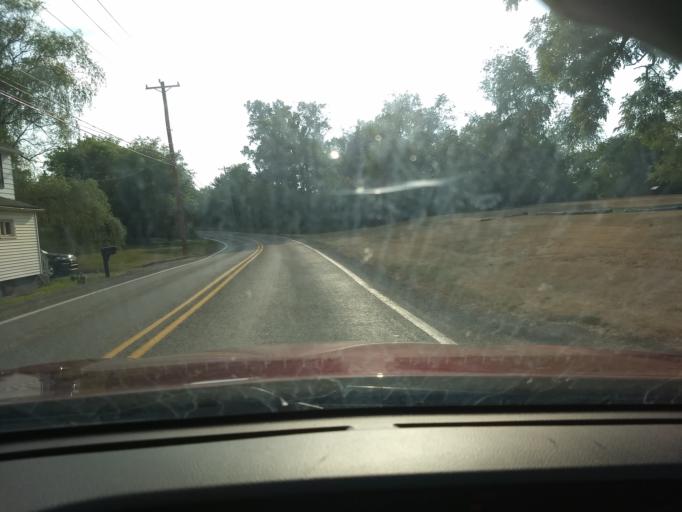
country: US
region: Pennsylvania
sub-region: Allegheny County
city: Curtisville
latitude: 40.6311
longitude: -79.8845
